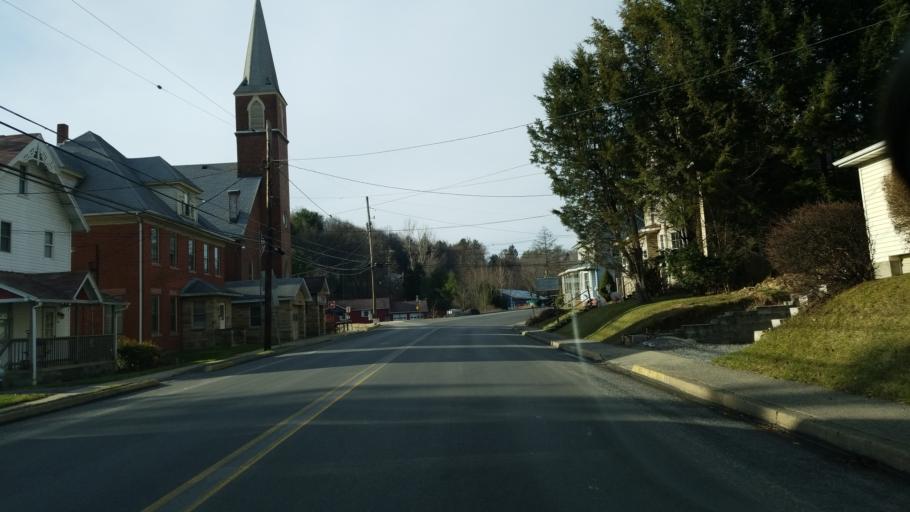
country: US
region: Pennsylvania
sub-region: Clearfield County
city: Curwensville
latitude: 40.9665
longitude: -78.6156
